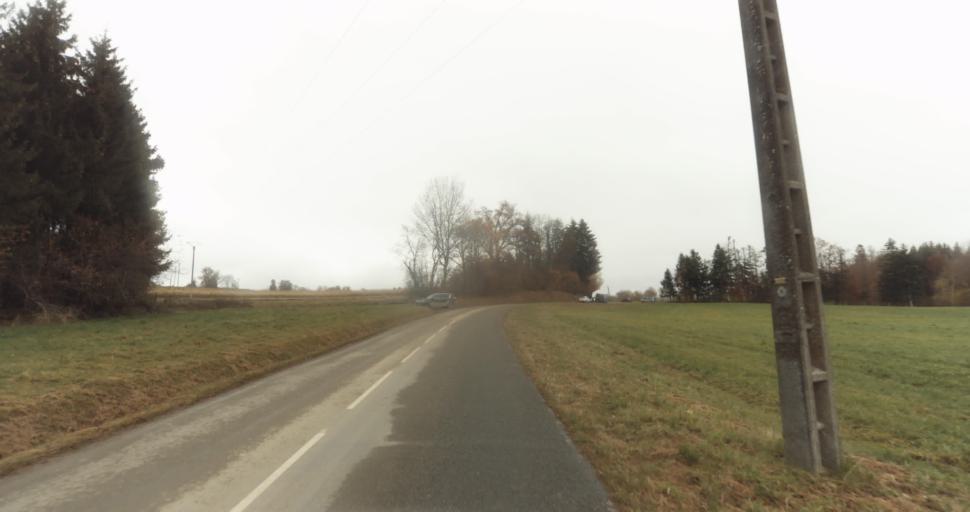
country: FR
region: Rhone-Alpes
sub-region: Departement de la Haute-Savoie
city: Evires
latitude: 46.0480
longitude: 6.2254
